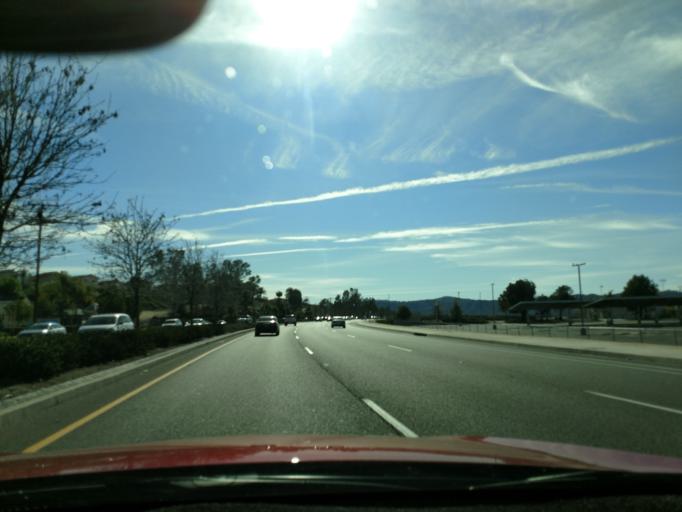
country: US
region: California
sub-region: Riverside County
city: Murrieta Hot Springs
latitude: 33.5383
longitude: -117.1450
